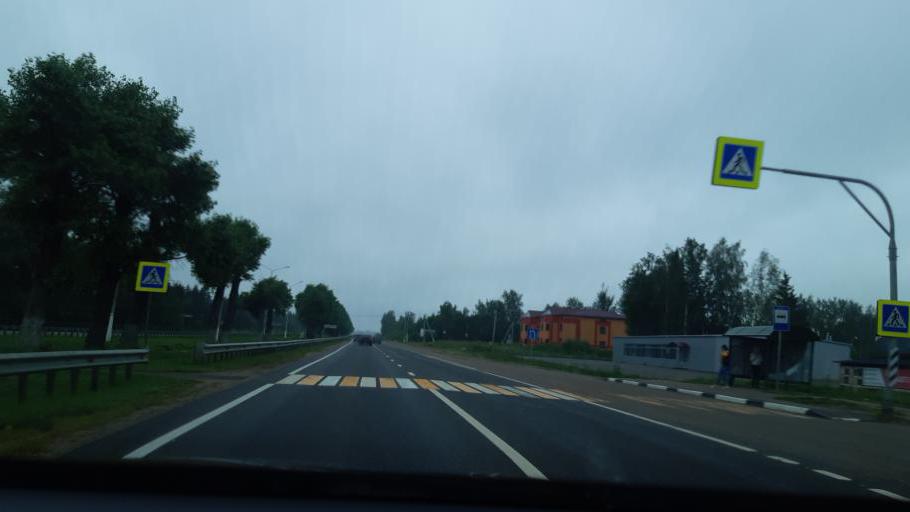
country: RU
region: Smolensk
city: Talashkino
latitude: 54.6852
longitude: 32.1367
